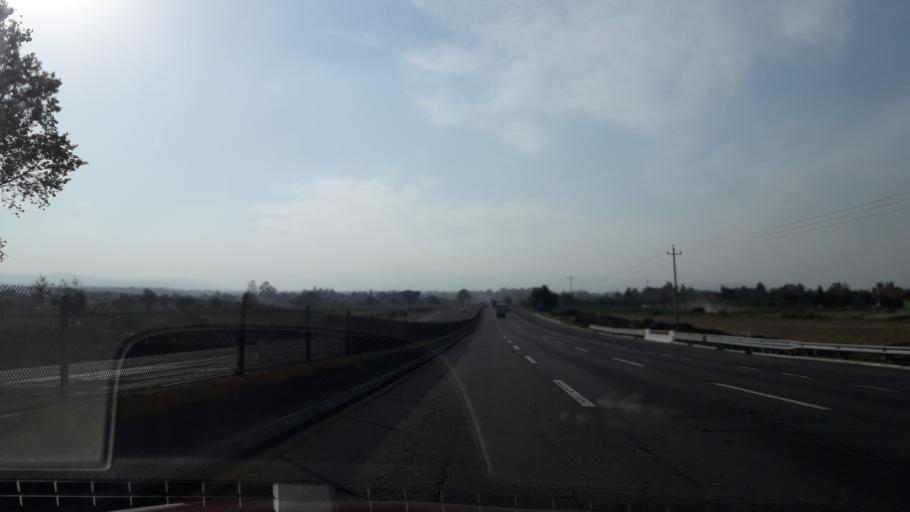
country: MX
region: Puebla
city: San Matias Tlalancaleca
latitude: 19.3095
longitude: -98.4964
